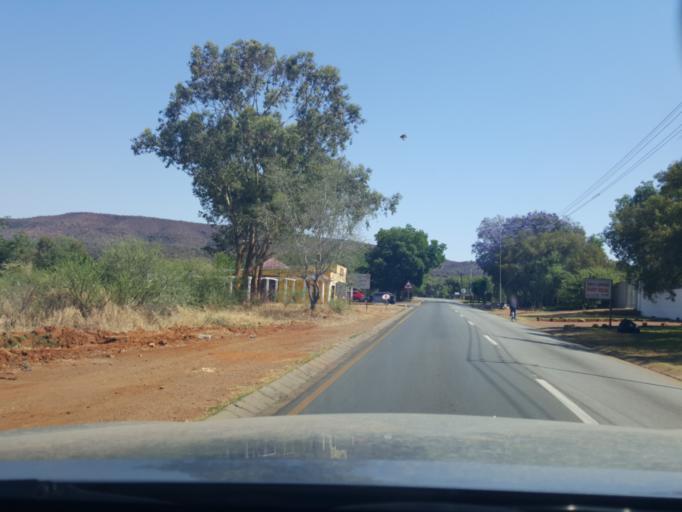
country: ZA
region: North-West
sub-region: Ngaka Modiri Molema District Municipality
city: Zeerust
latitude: -25.5271
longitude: 26.0749
